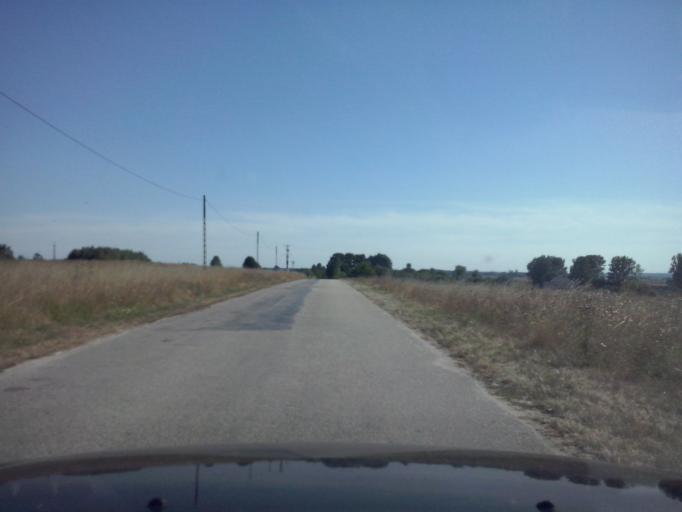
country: PL
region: Swietokrzyskie
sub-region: Powiat pinczowski
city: Kije
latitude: 50.5994
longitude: 20.6424
